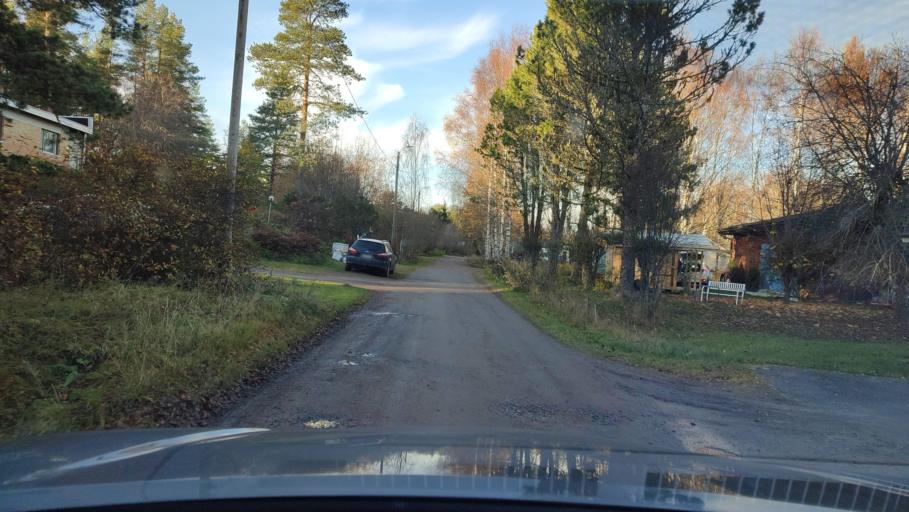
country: FI
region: Ostrobothnia
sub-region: Vaasa
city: Teeriniemi
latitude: 63.0677
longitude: 21.6957
